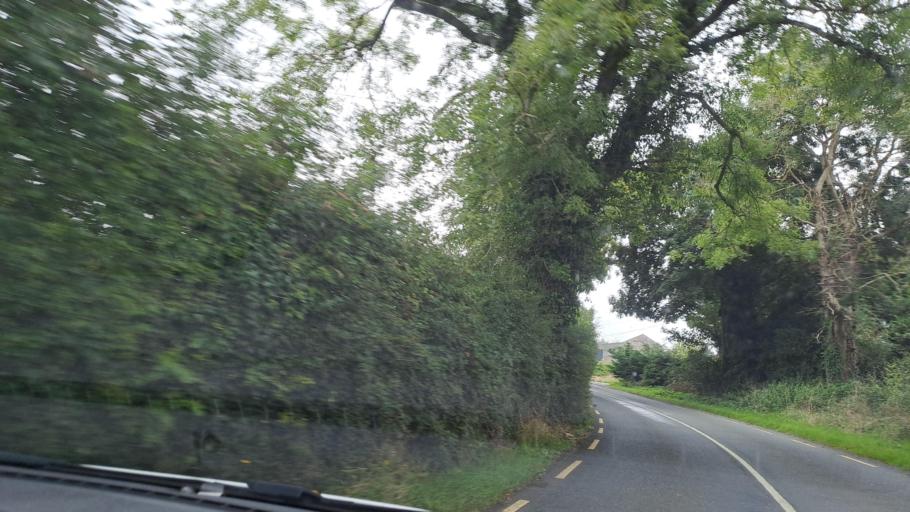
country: IE
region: Ulster
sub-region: County Monaghan
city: Carrickmacross
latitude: 54.0186
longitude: -6.7128
